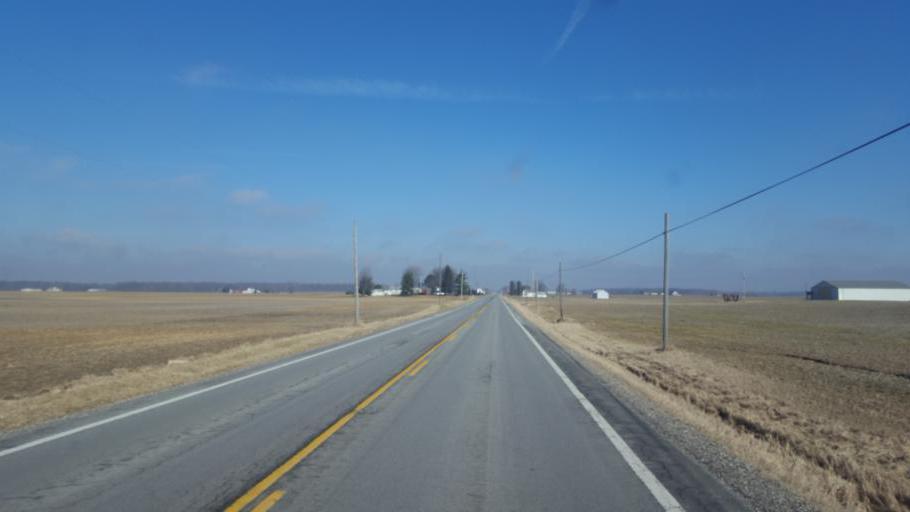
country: US
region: Ohio
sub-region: Crawford County
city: Bucyrus
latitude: 40.9097
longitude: -82.9543
